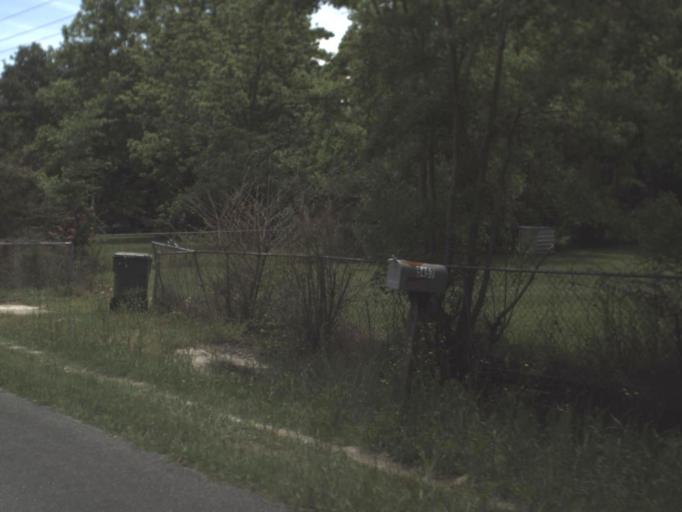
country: US
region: Florida
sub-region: Gulf County
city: Wewahitchka
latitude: 30.2006
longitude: -85.2081
